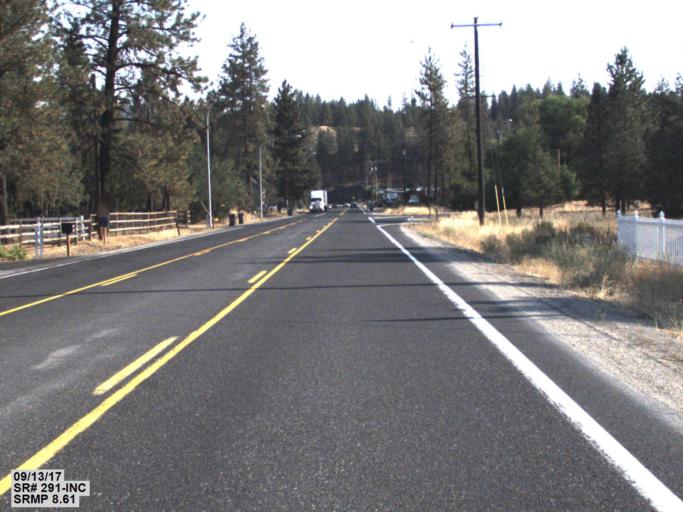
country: US
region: Washington
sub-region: Spokane County
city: Fairwood
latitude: 47.7695
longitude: -117.5460
